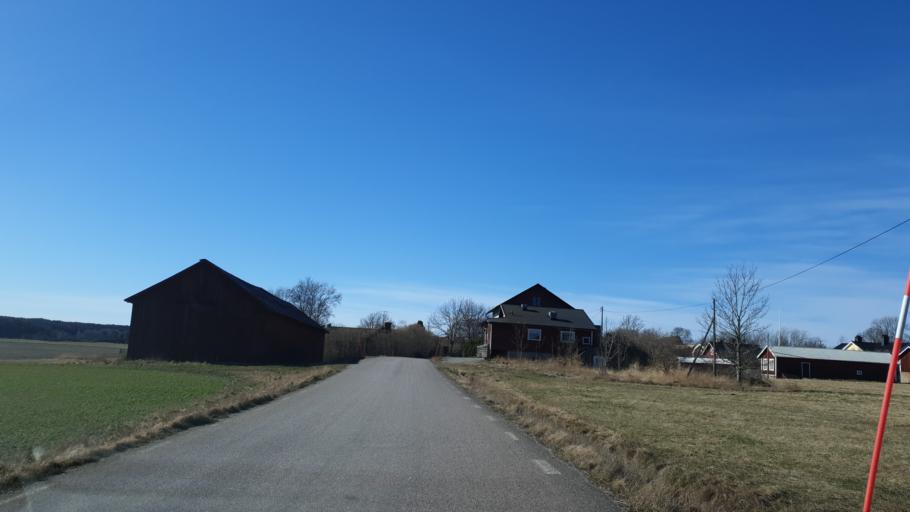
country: SE
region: Uppsala
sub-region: Enkopings Kommun
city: Dalby
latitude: 59.5210
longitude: 17.2779
